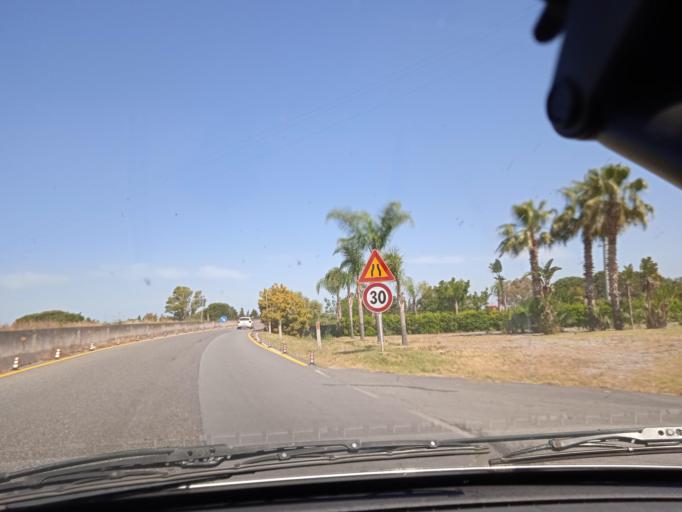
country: IT
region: Sicily
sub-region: Messina
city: San Filippo del Mela
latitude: 38.1856
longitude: 15.2651
